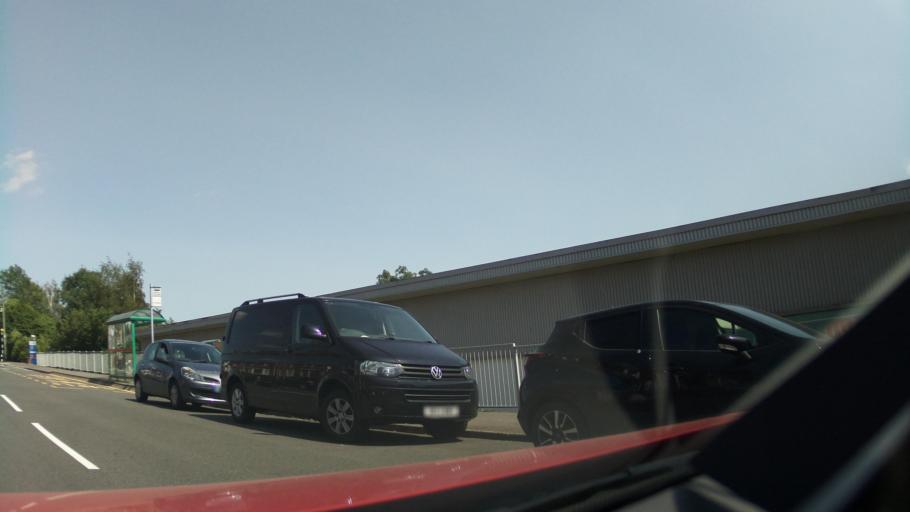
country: GB
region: Wales
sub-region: Caerphilly County Borough
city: Ystrad Mynach
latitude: 51.6426
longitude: -3.2326
